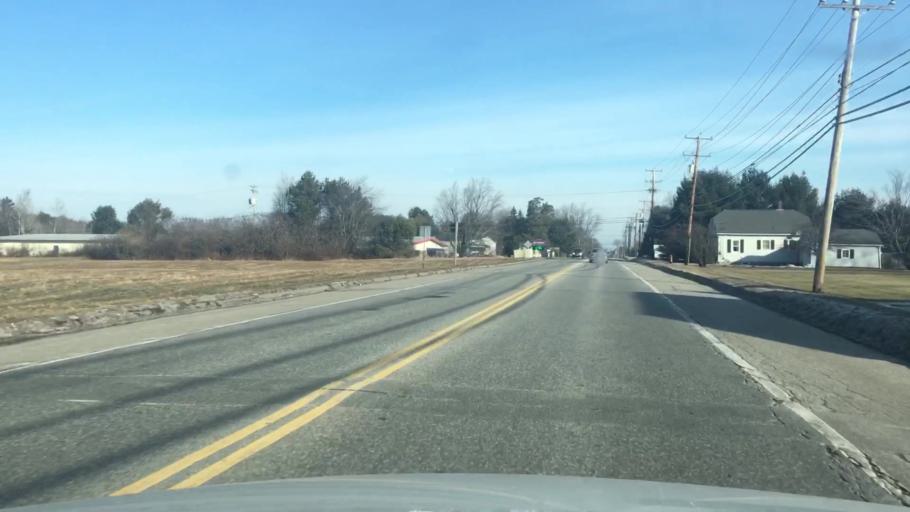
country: US
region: Maine
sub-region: Androscoggin County
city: Auburn
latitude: 44.0666
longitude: -70.2704
